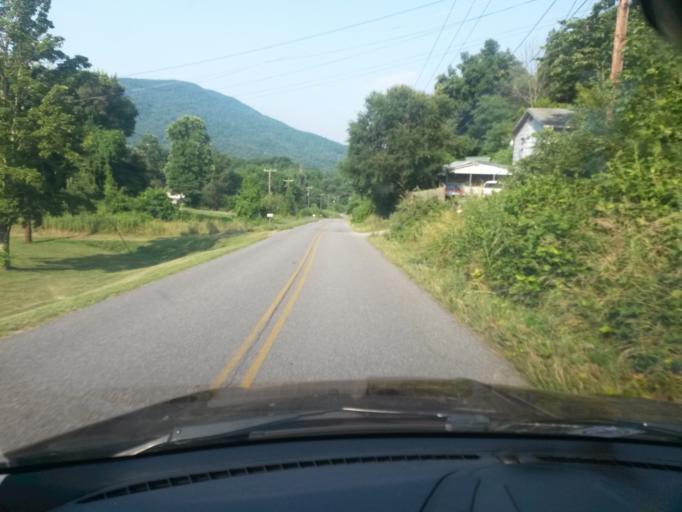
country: US
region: Virginia
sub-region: Giles County
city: Narrows
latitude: 37.3699
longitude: -80.8063
